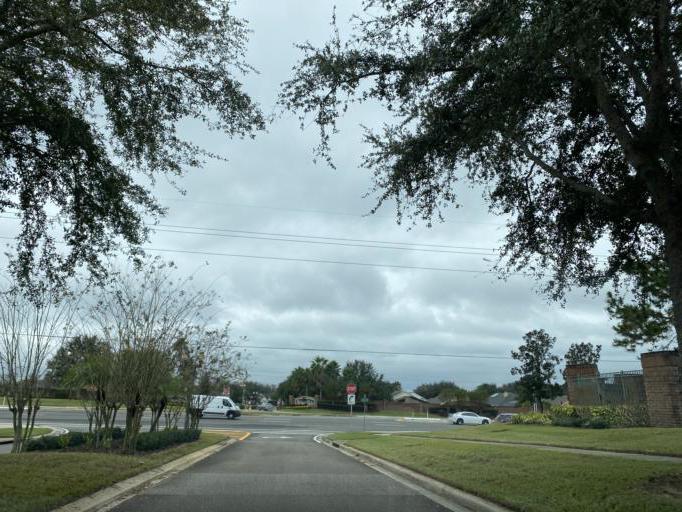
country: US
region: Florida
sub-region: Lake County
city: Four Corners
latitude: 28.3944
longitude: -81.6929
